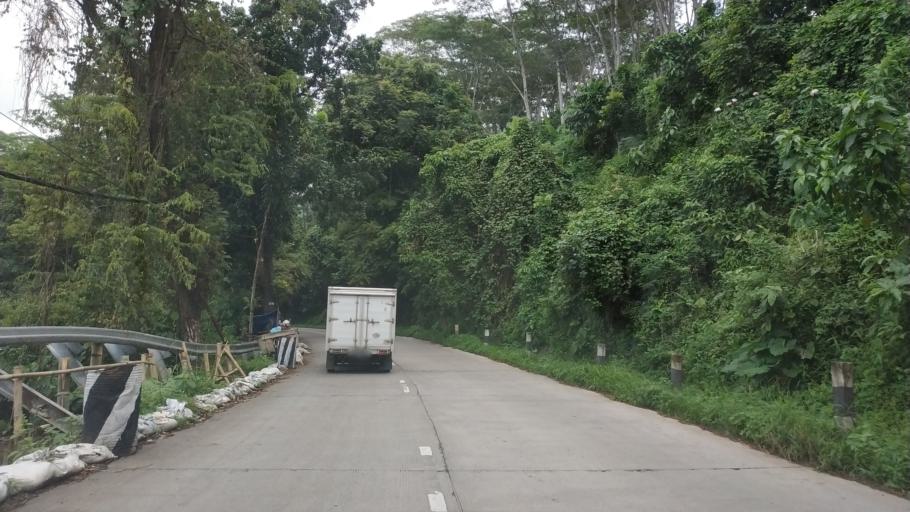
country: ID
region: Central Java
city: Weleri
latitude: -7.0024
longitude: 110.0612
